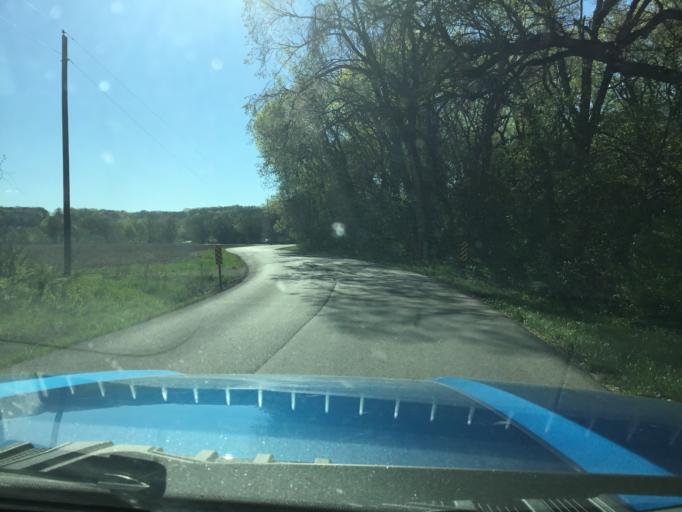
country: US
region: Kansas
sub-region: Douglas County
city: Lawrence
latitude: 38.9939
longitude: -95.3074
